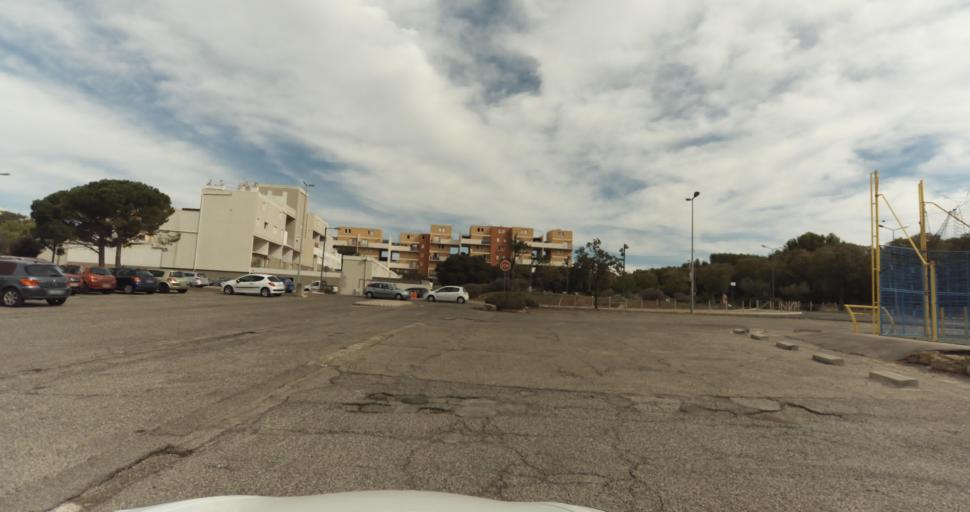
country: FR
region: Provence-Alpes-Cote d'Azur
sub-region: Departement des Bouches-du-Rhone
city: Miramas
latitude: 43.5944
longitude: 5.0106
